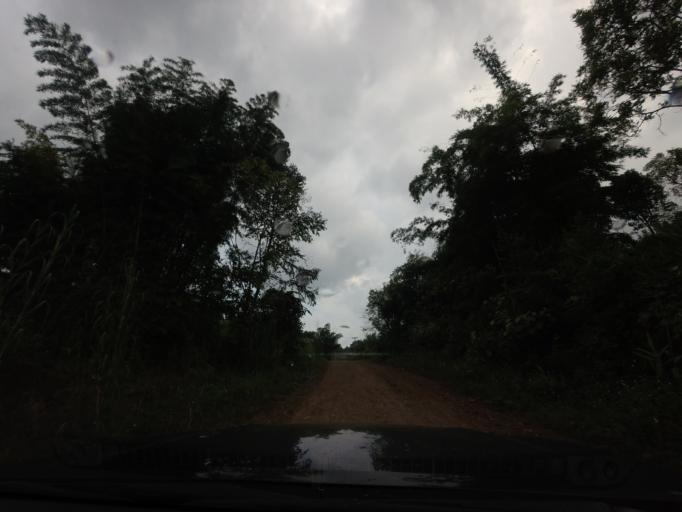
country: TH
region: Nan
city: Bo Kluea
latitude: 19.3521
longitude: 101.1735
